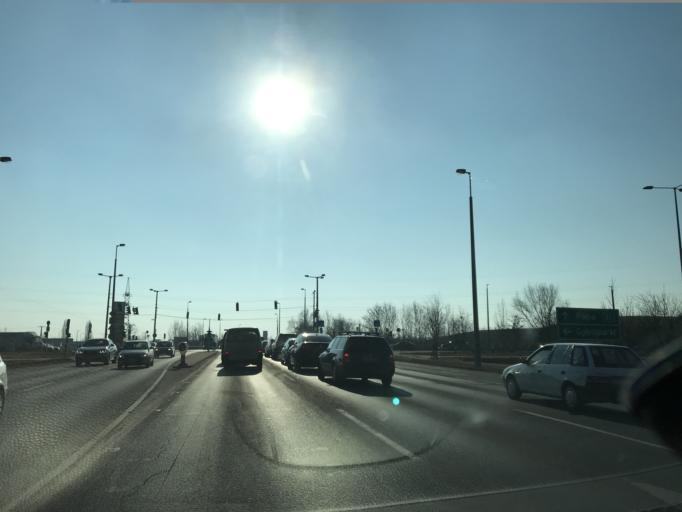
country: HU
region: Gyor-Moson-Sopron
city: Gyor
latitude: 47.6549
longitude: 17.6327
